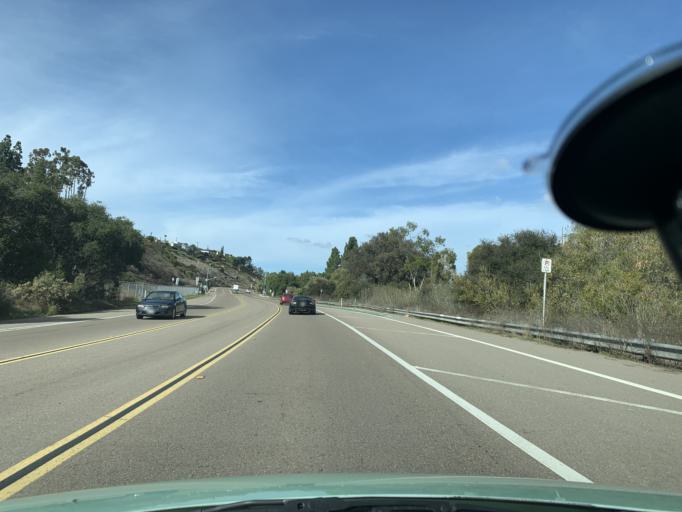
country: US
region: California
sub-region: San Diego County
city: San Diego
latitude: 32.8033
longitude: -117.1743
